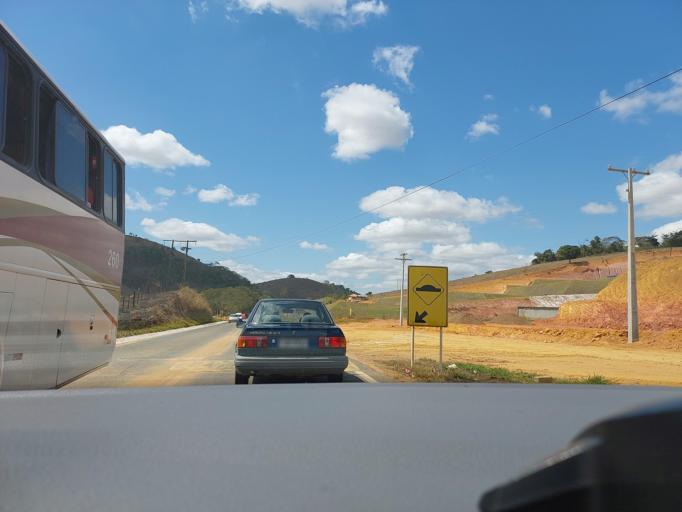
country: BR
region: Minas Gerais
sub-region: Muriae
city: Muriae
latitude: -21.1134
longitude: -42.4405
